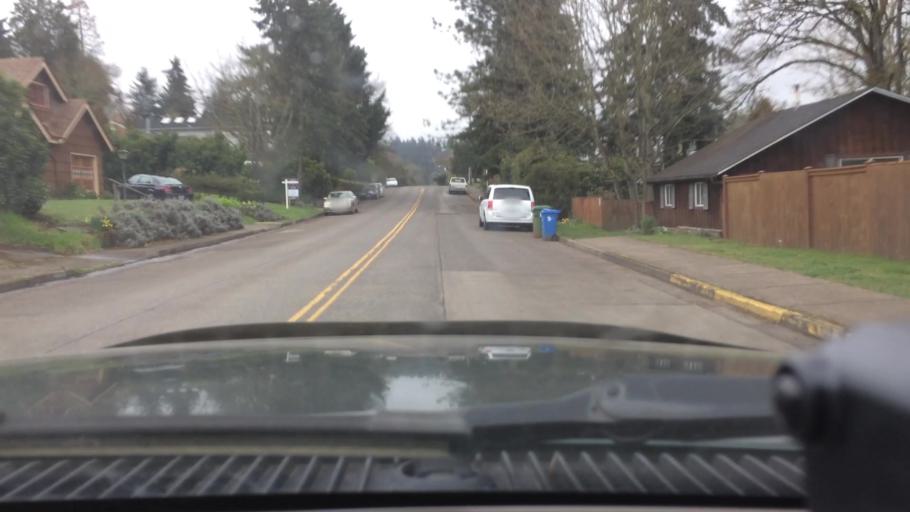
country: US
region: Oregon
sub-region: Lane County
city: Eugene
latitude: 44.0332
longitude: -123.1013
